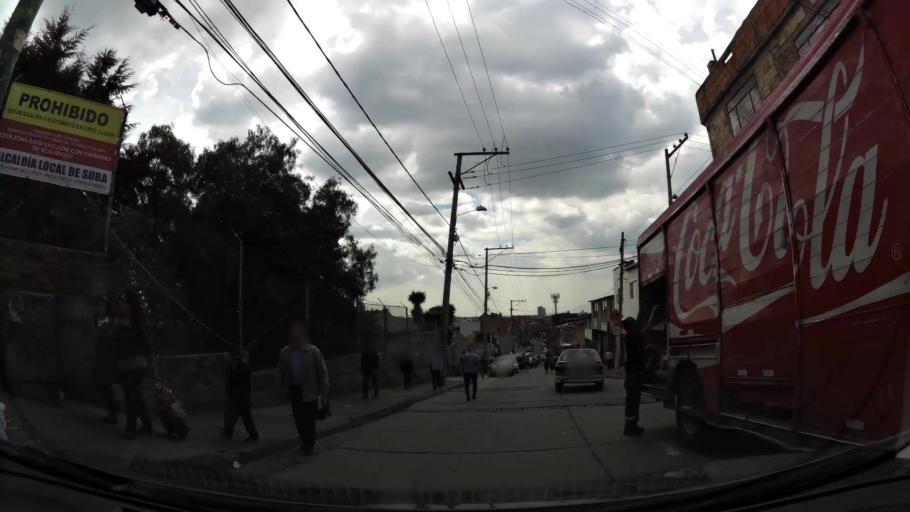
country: CO
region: Bogota D.C.
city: Barrio San Luis
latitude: 4.7231
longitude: -74.0875
